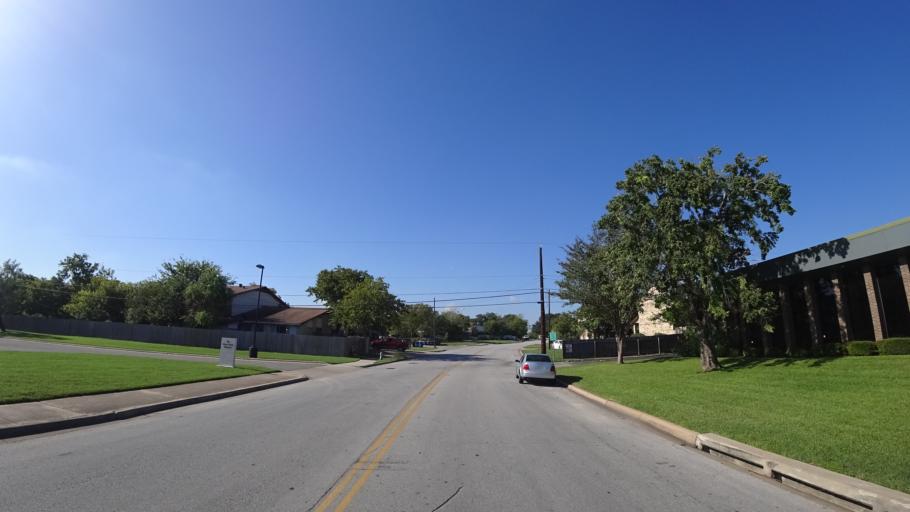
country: US
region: Texas
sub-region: Travis County
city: Austin
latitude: 30.3428
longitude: -97.7061
